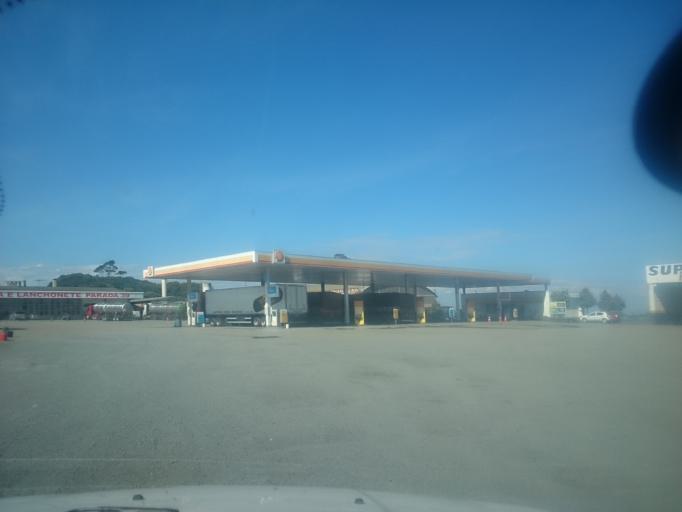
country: BR
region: Parana
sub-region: Campo Largo
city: Campo Largo
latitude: -25.4720
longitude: -49.6692
